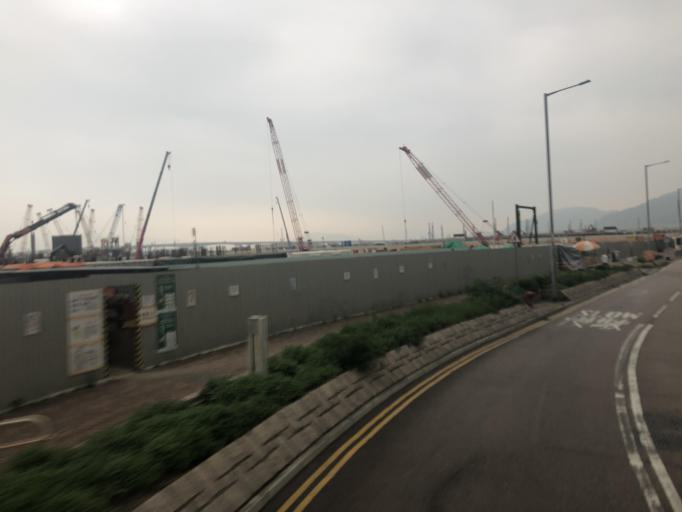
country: HK
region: Tuen Mun
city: Tuen Mun
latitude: 22.2970
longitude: 113.9520
